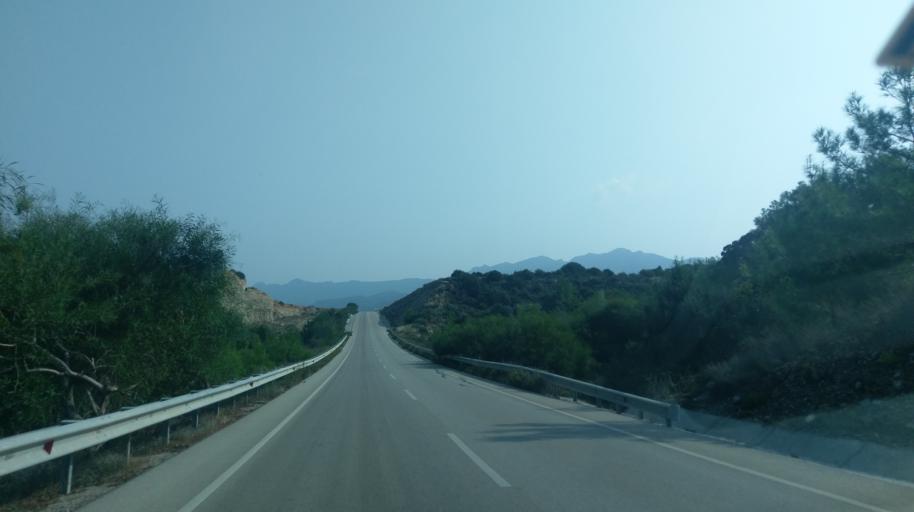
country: CY
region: Ammochostos
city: Trikomo
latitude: 35.4108
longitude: 33.8079
